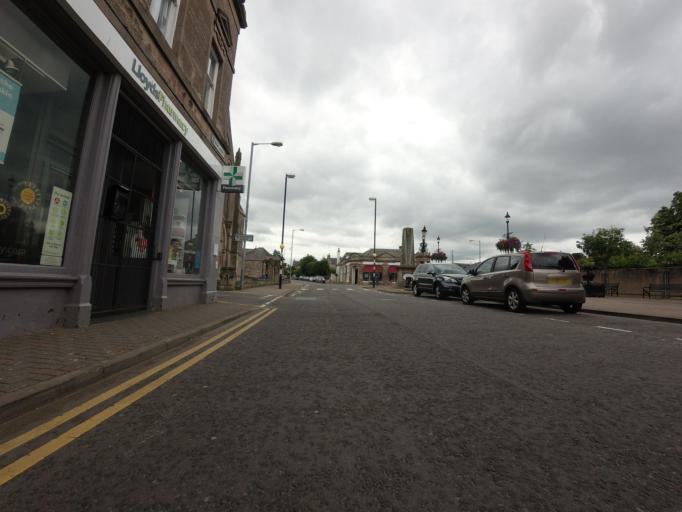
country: GB
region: Scotland
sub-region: Highland
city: Nairn
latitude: 57.5833
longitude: -3.8707
